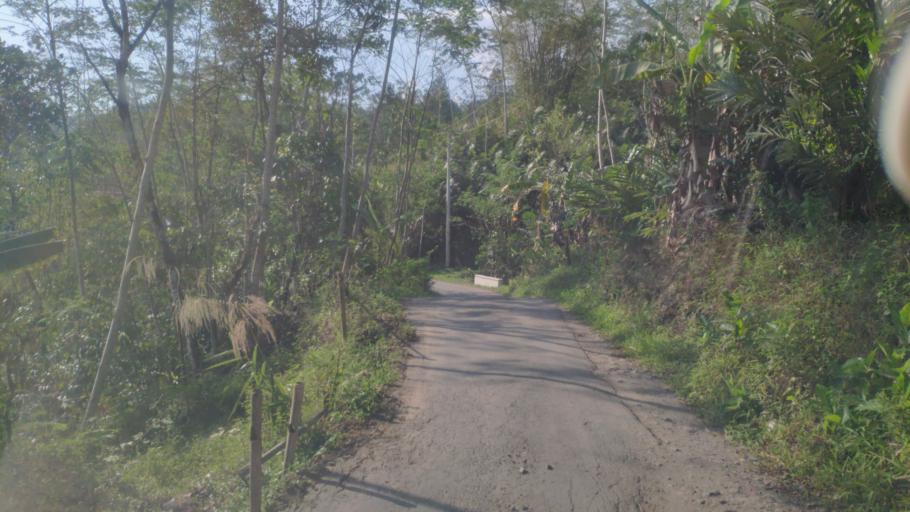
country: ID
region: Central Java
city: Buaran
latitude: -7.2425
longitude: 109.5867
